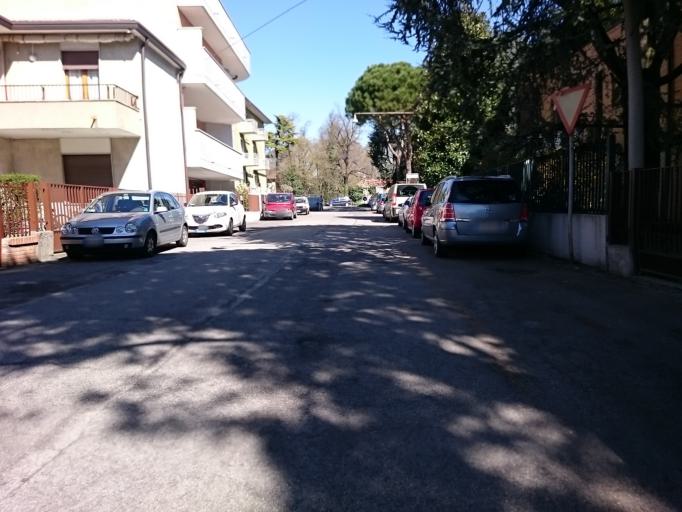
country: IT
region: Veneto
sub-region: Provincia di Padova
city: Padova
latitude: 45.4033
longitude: 11.8954
